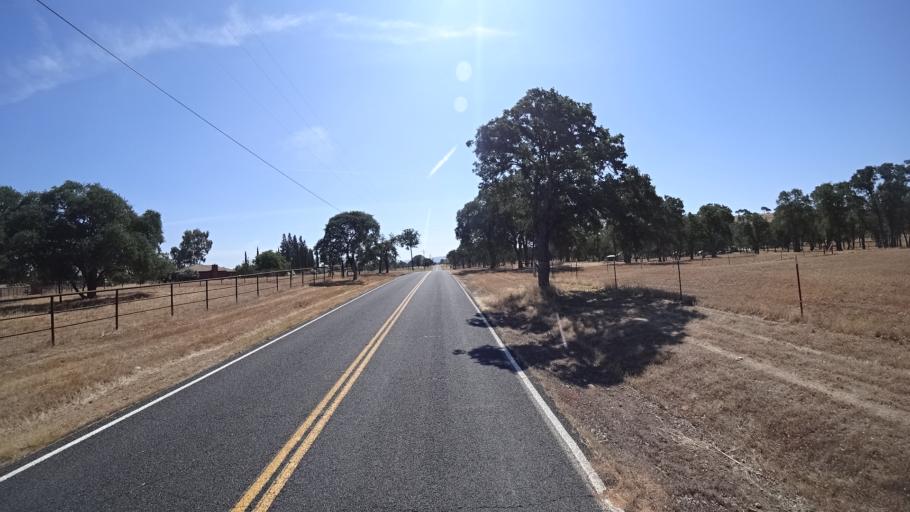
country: US
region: California
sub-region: Calaveras County
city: Rancho Calaveras
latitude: 38.1339
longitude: -120.9201
